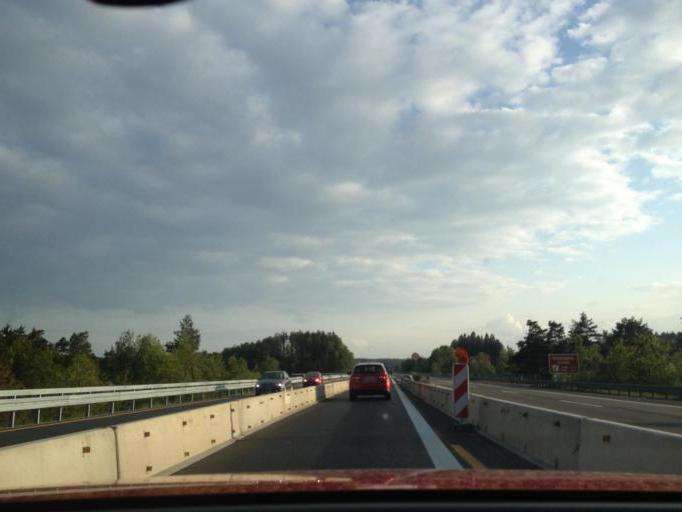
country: DE
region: Bavaria
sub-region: Upper Palatinate
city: Windischeschenbach
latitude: 49.7865
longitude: 12.1682
